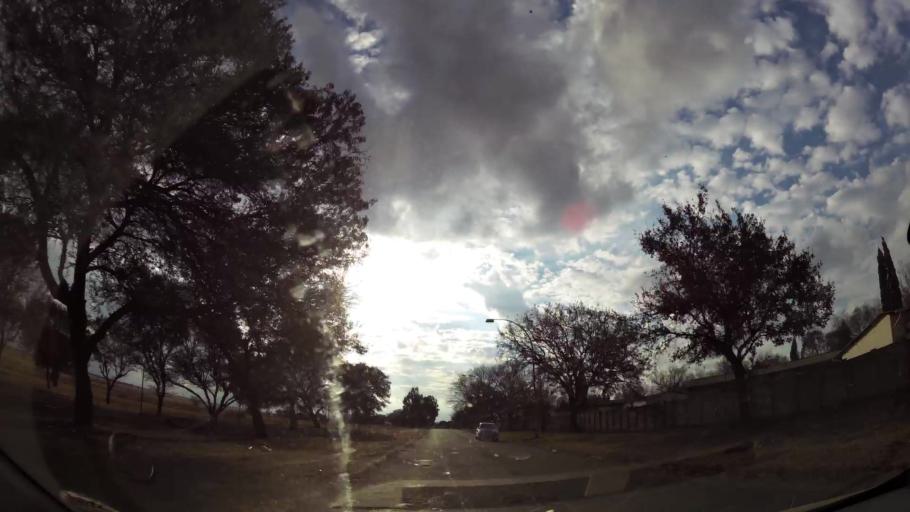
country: ZA
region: Orange Free State
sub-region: Fezile Dabi District Municipality
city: Sasolburg
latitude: -26.8243
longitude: 27.8122
